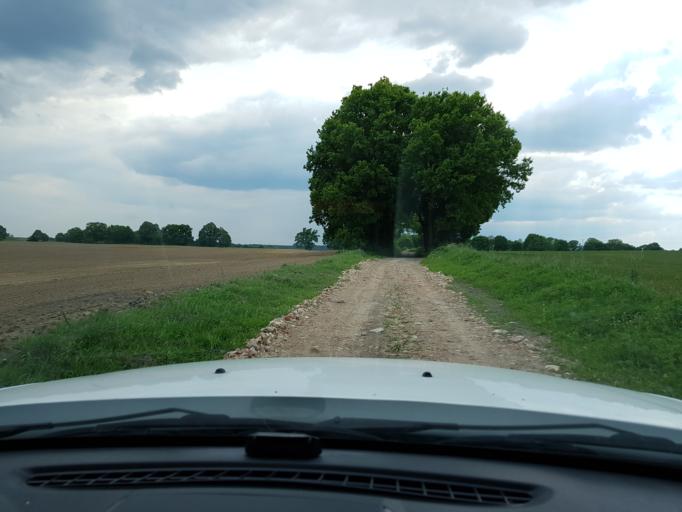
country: PL
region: West Pomeranian Voivodeship
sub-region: Powiat drawski
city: Drawsko Pomorskie
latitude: 53.5403
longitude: 15.7355
